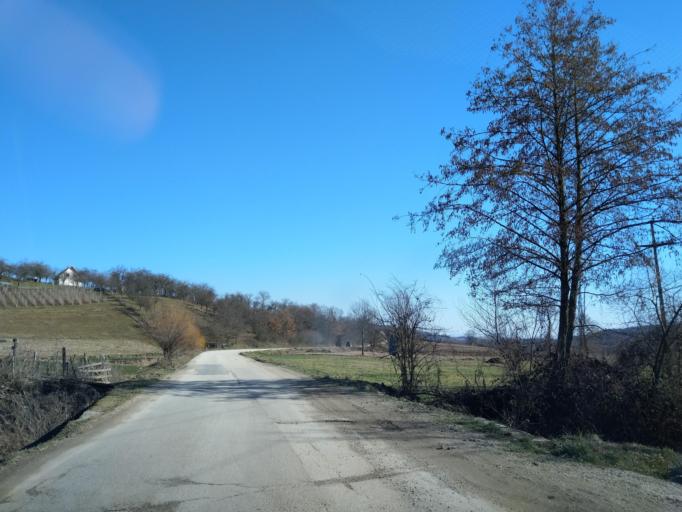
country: RS
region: Central Serbia
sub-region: Zlatiborski Okrug
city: Kosjeric
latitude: 43.9384
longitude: 19.8775
